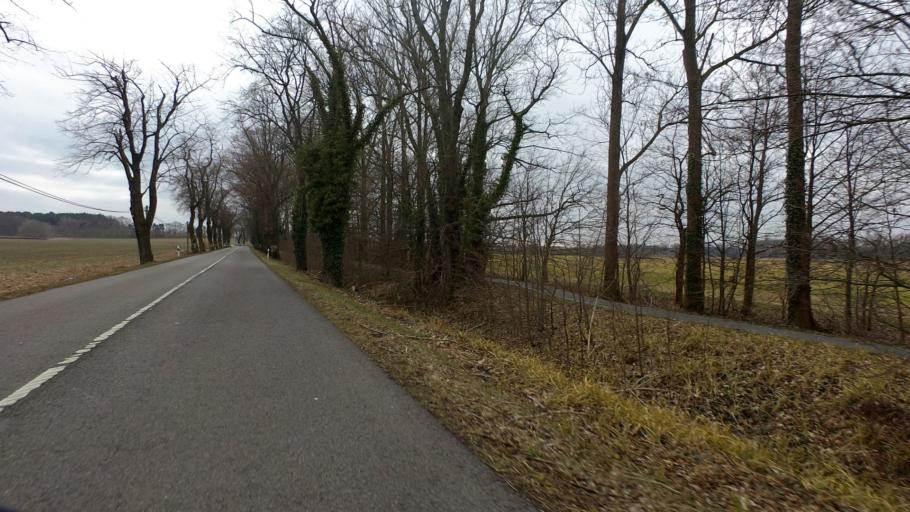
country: DE
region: Brandenburg
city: Trebbin
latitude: 52.2075
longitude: 13.2103
